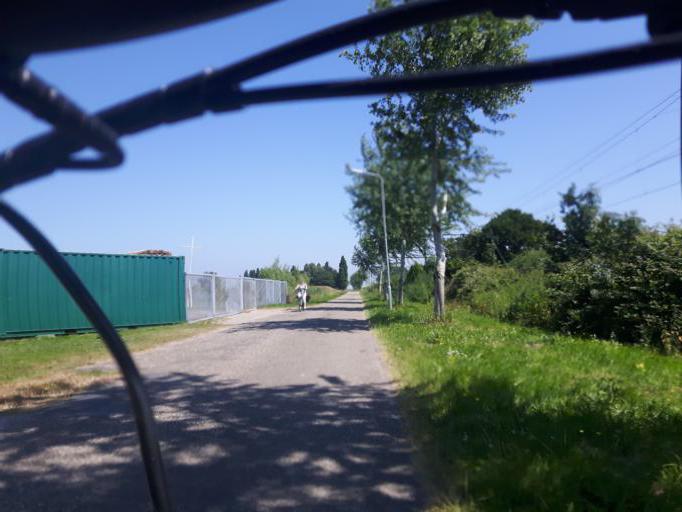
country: NL
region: Zeeland
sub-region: Gemeente Veere
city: Veere
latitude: 51.5028
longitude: 3.6808
